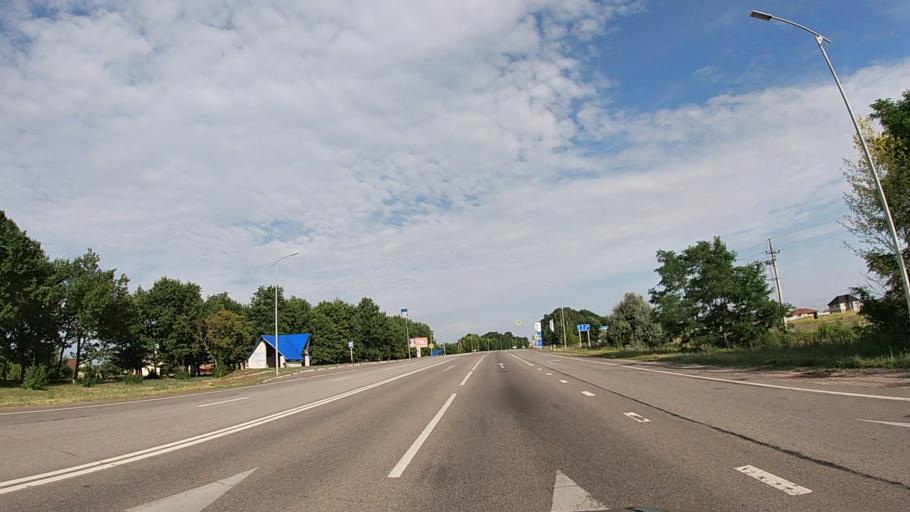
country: RU
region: Belgorod
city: Severnyy
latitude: 50.6380
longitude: 36.4448
